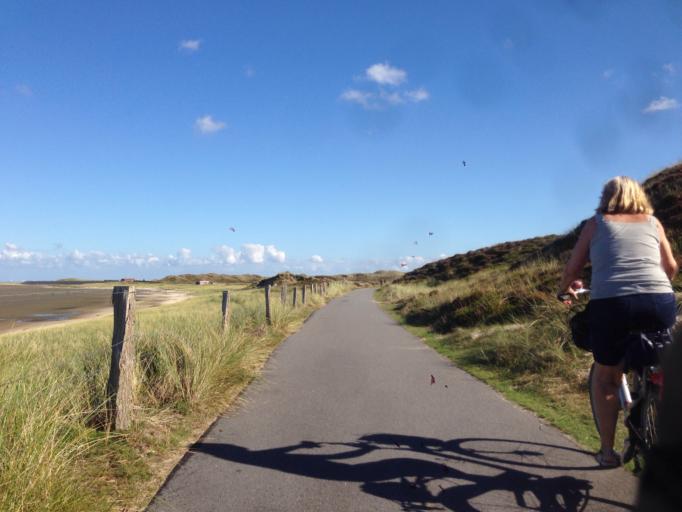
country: DE
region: Schleswig-Holstein
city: List
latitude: 55.0349
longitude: 8.3991
